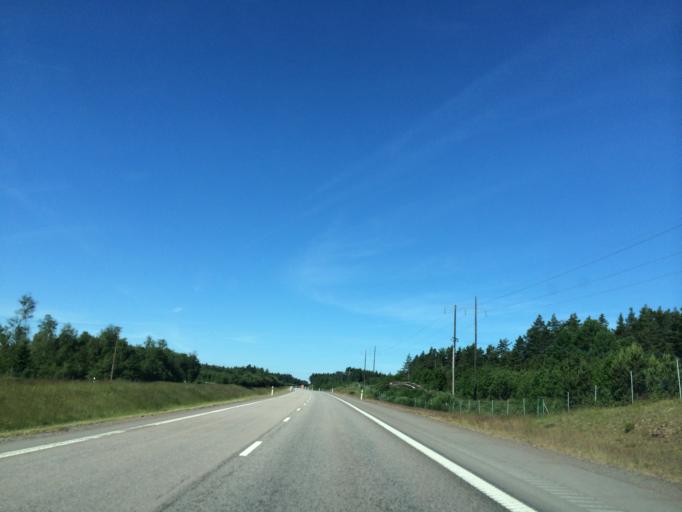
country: SE
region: OEstergoetland
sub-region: Vadstena Kommun
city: Herrestad
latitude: 58.2513
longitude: 14.7982
